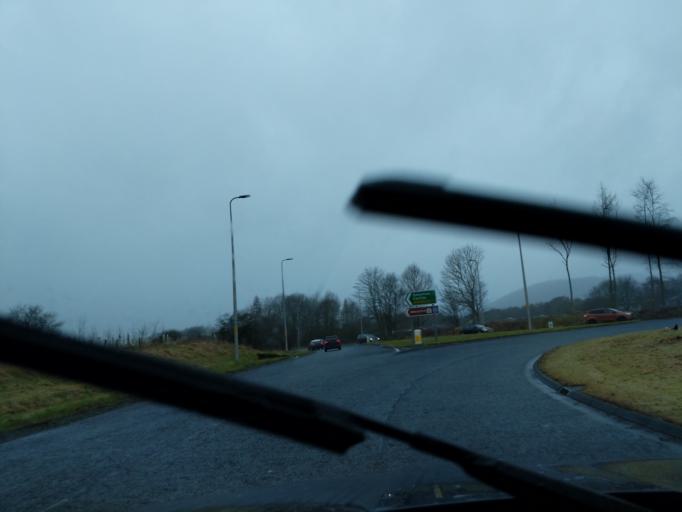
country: GB
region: Scotland
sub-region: The Scottish Borders
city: Melrose
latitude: 55.6012
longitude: -2.7513
